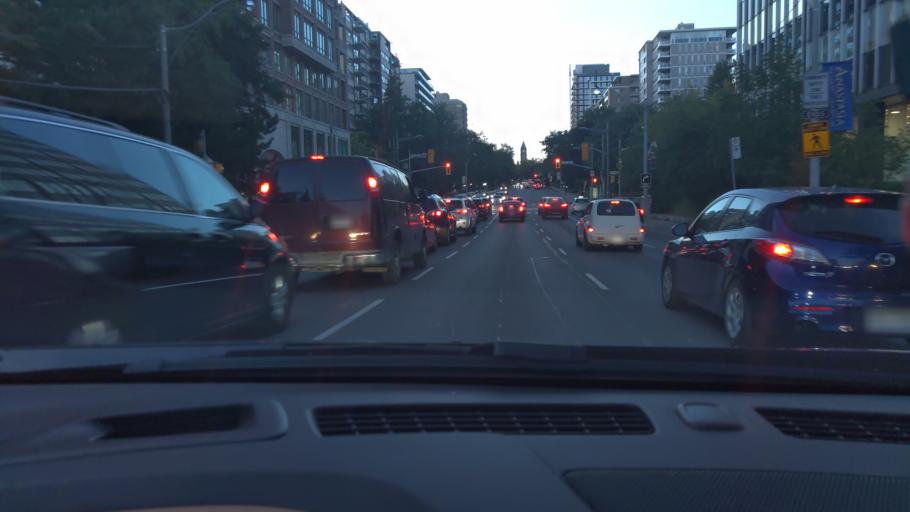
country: CA
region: Ontario
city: Toronto
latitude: 43.6858
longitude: -79.4011
